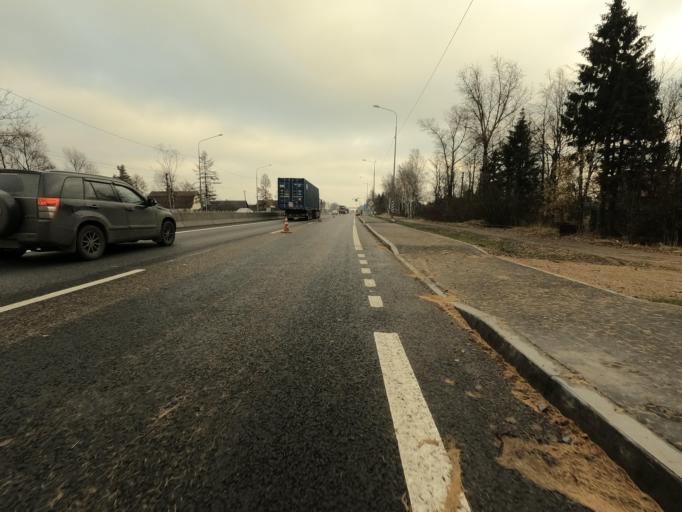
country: RU
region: Leningrad
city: Mga
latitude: 59.7237
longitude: 31.0958
